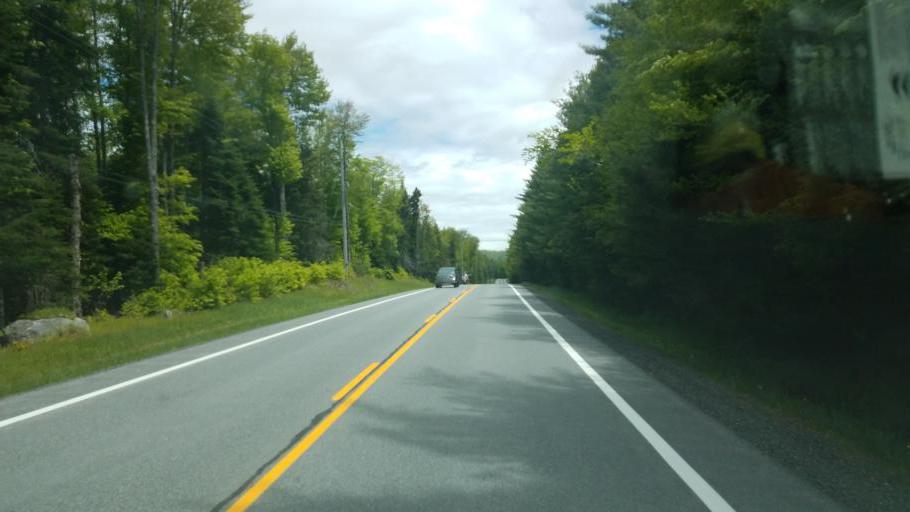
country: US
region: New York
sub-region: Hamilton County
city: Lake Pleasant
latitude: 43.8227
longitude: -74.5833
